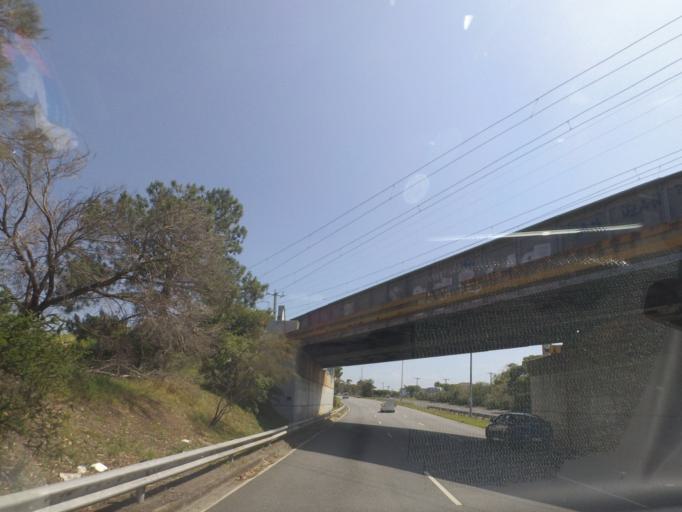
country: AU
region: Victoria
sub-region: Kingston
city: Mordialloc
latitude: -38.0013
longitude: 145.0837
